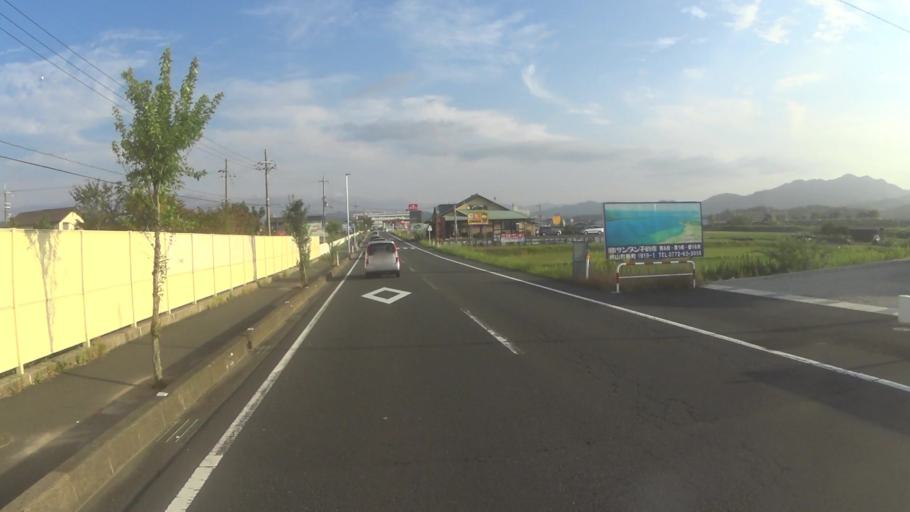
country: JP
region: Kyoto
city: Miyazu
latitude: 35.6139
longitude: 135.0787
